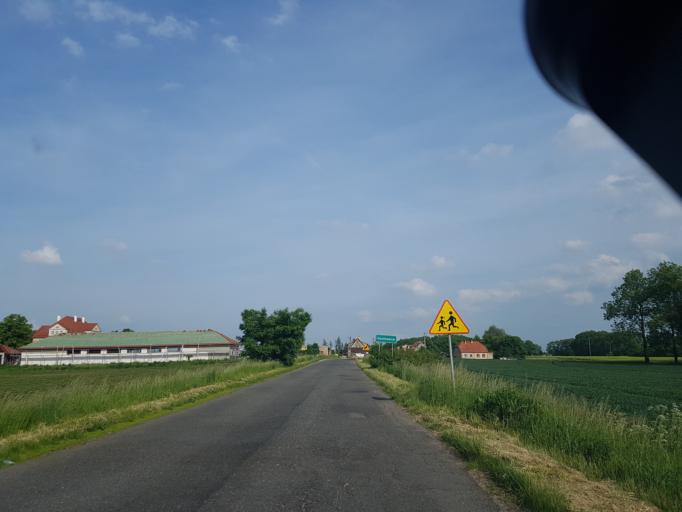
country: PL
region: Lower Silesian Voivodeship
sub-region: Powiat wroclawski
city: Zorawina
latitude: 50.9088
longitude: 17.0847
